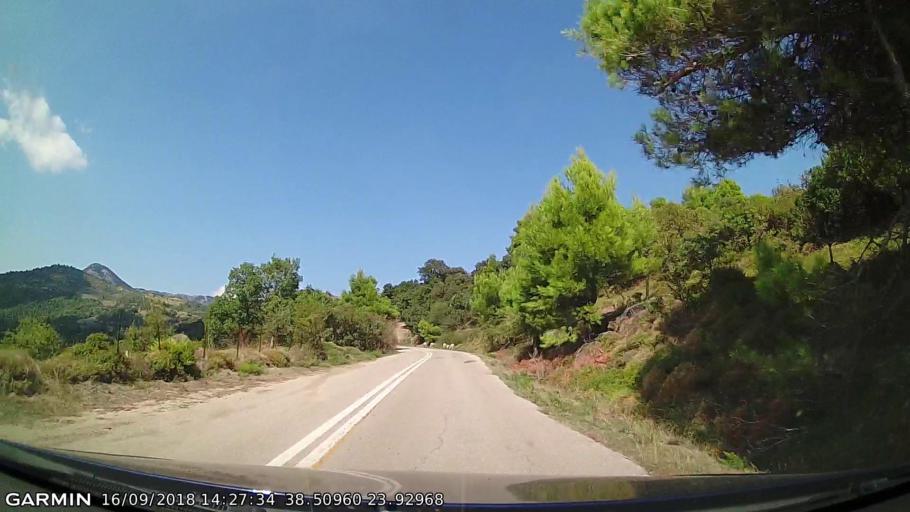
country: GR
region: Central Greece
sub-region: Nomos Evvoias
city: Yimnon
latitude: 38.5096
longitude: 23.9297
